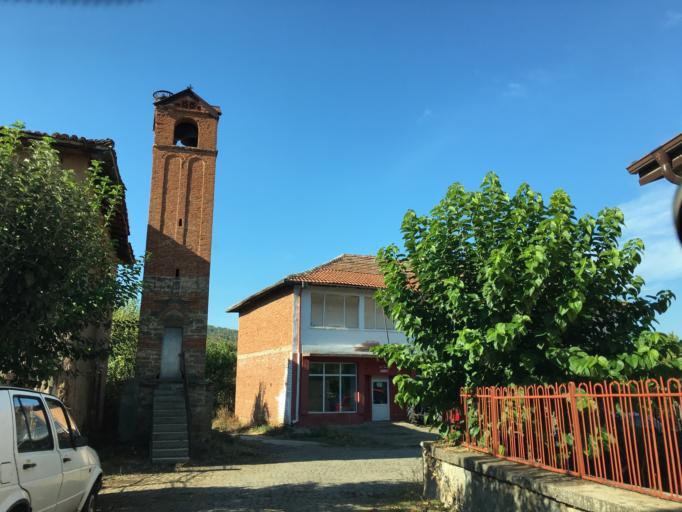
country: BG
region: Khaskovo
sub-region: Obshtina Ivaylovgrad
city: Ivaylovgrad
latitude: 41.3915
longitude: 26.1325
